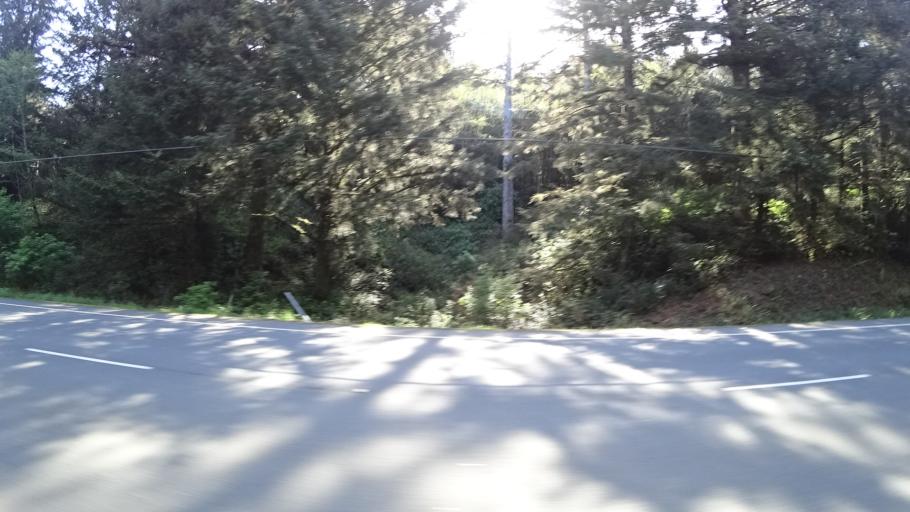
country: US
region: Oregon
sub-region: Curry County
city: Gold Beach
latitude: 42.2425
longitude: -124.3920
